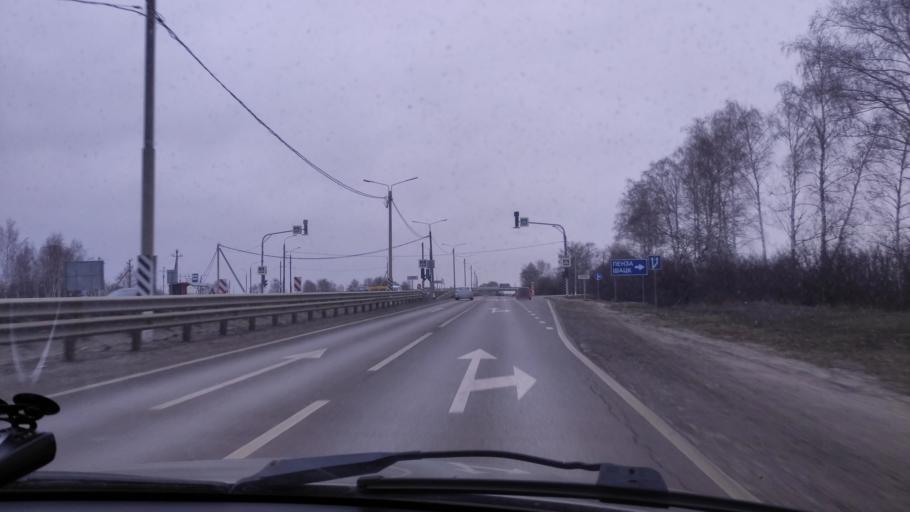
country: RU
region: Tambov
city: Komsomolets
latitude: 52.7327
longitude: 41.3027
